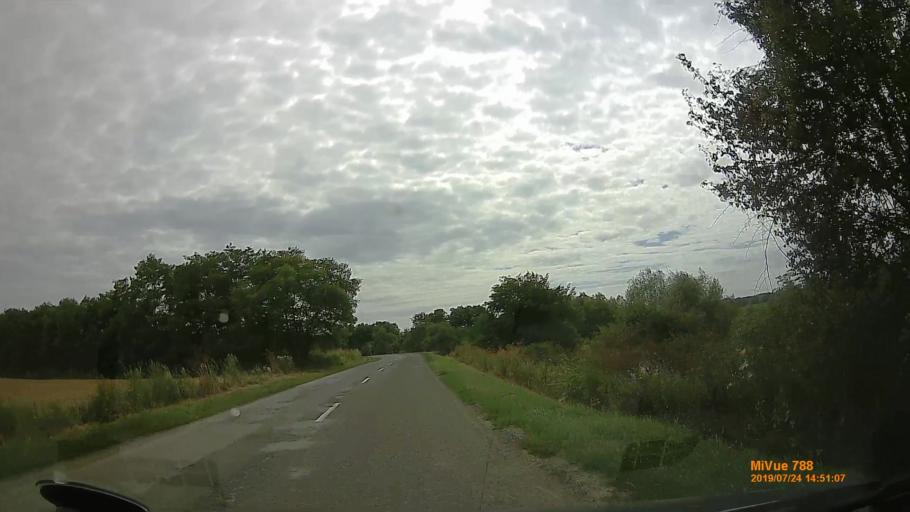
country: HU
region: Szabolcs-Szatmar-Bereg
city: Aranyosapati
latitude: 48.2750
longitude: 22.2855
